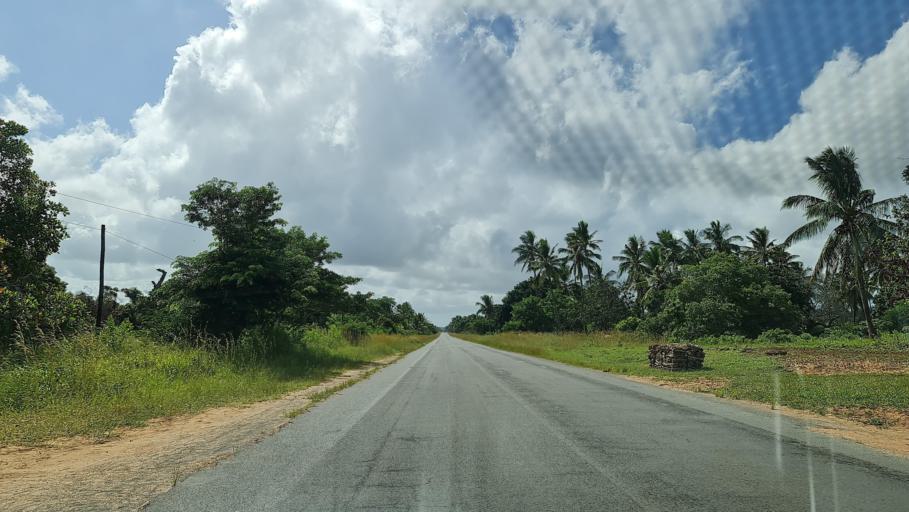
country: MZ
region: Gaza
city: Manjacaze
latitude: -24.6798
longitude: 34.6016
